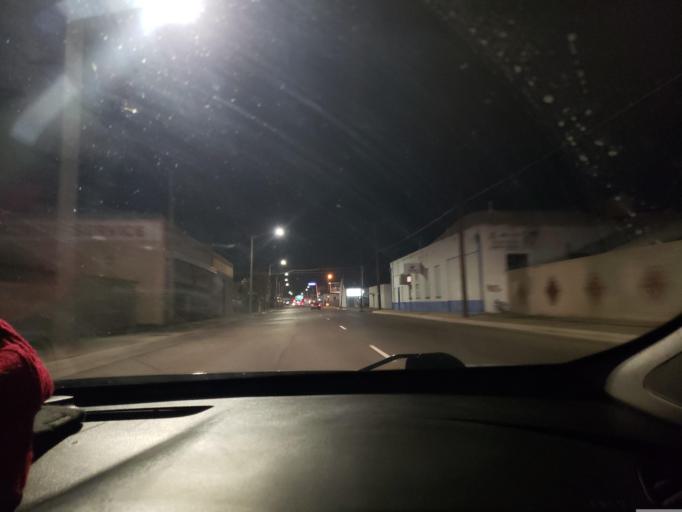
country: US
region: New Mexico
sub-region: Bernalillo County
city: Albuquerque
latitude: 35.1005
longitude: -106.6462
